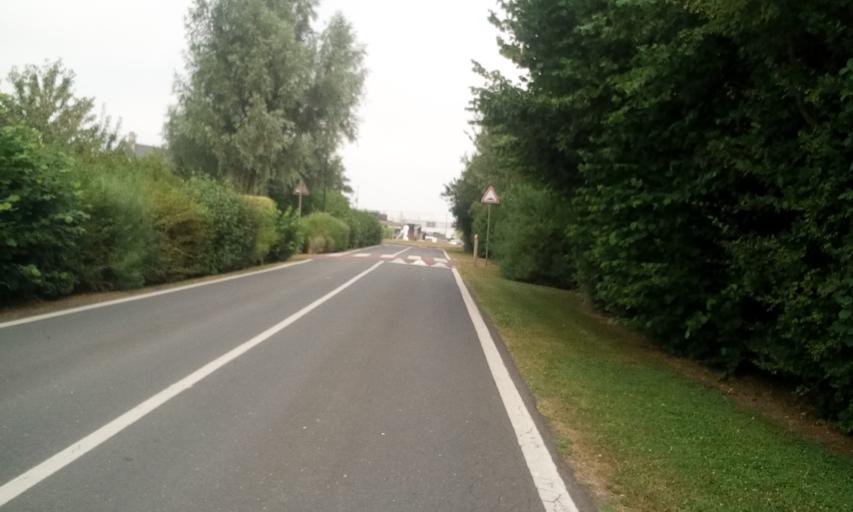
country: FR
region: Lower Normandy
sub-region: Departement du Calvados
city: Douvres-la-Delivrande
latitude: 49.2997
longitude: -0.3846
